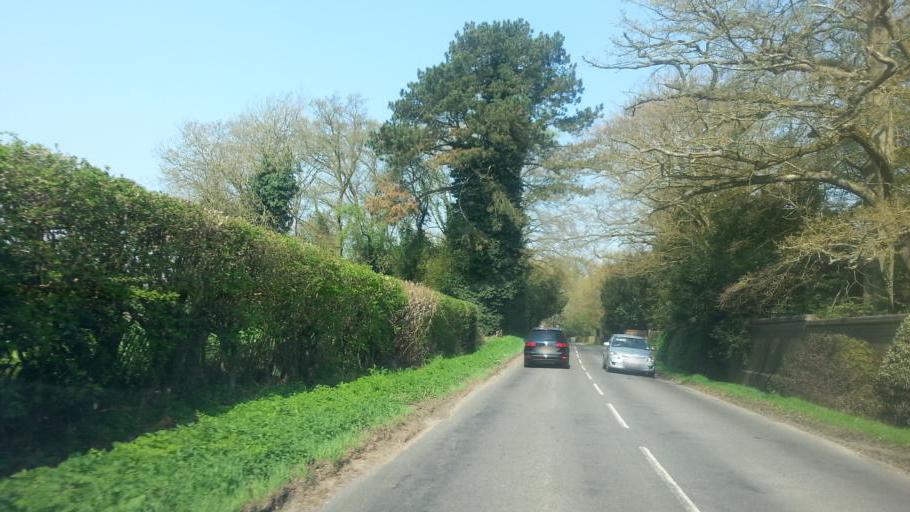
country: GB
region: England
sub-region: Suffolk
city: Thurston
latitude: 52.2454
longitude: 0.8169
